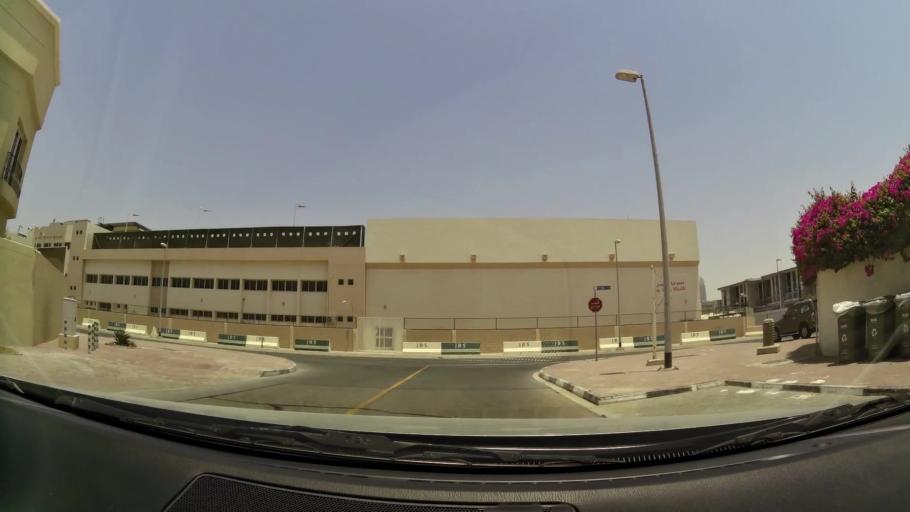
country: AE
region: Dubai
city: Dubai
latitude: 25.2185
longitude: 55.2584
